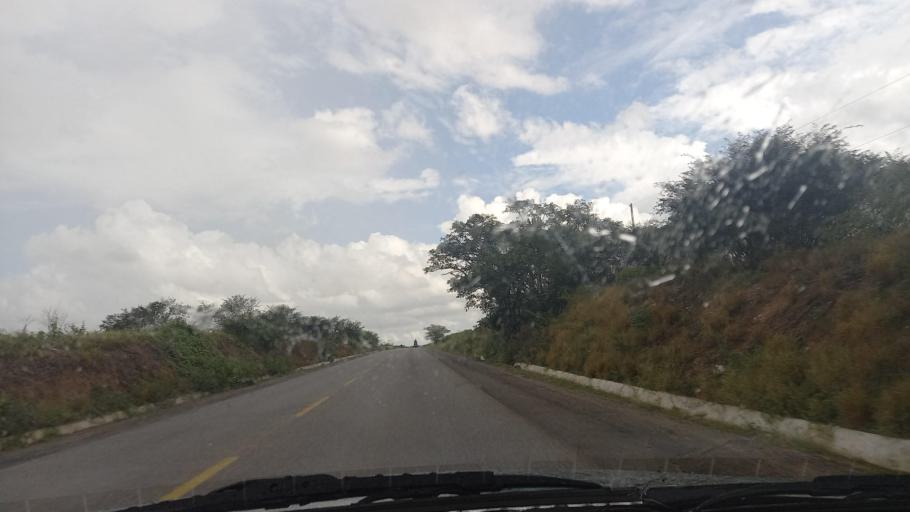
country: BR
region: Pernambuco
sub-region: Cachoeirinha
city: Cachoeirinha
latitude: -8.5577
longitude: -36.2753
